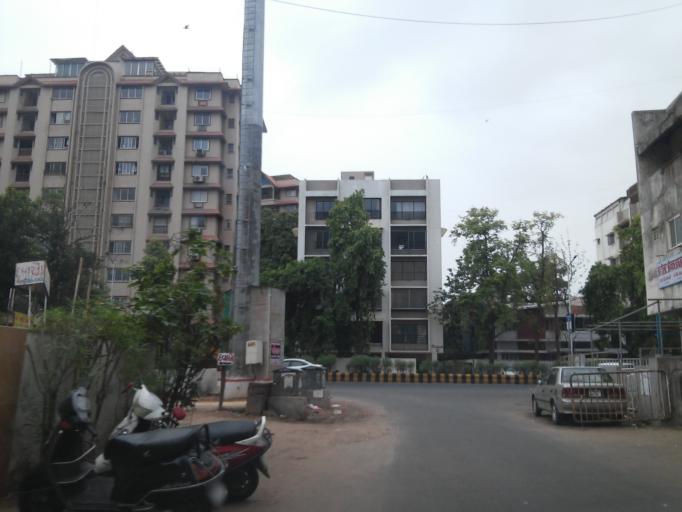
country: IN
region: Gujarat
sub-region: Ahmadabad
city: Ahmedabad
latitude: 23.0142
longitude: 72.5609
